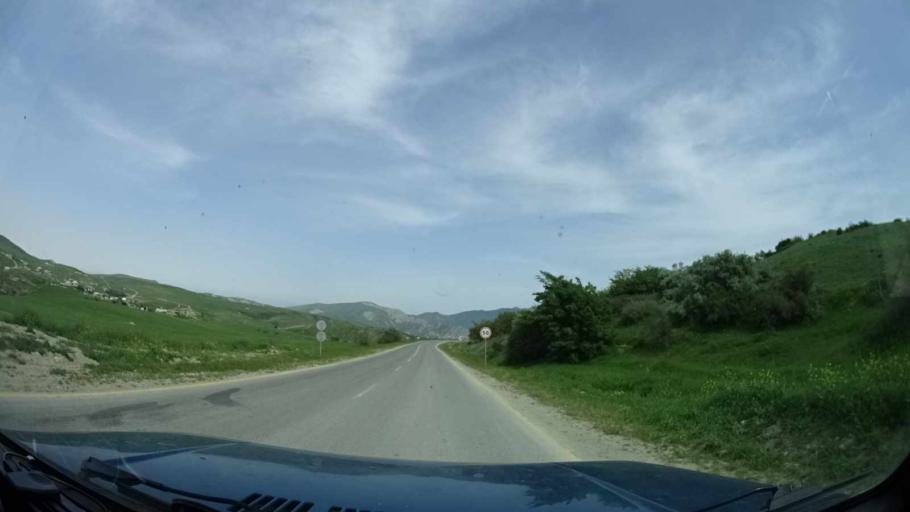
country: AZ
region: Xizi
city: Khyzy
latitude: 40.9073
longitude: 49.0954
